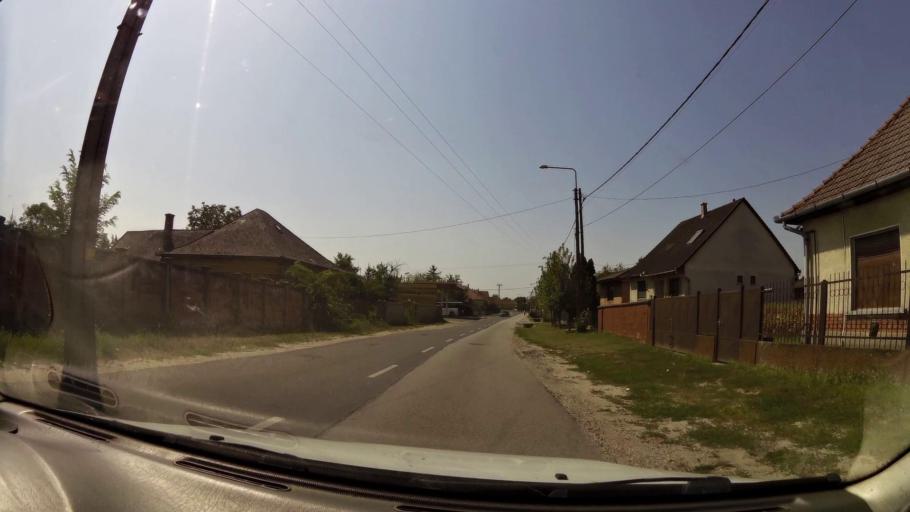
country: HU
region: Pest
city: Tapioszentmarton
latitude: 47.3460
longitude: 19.7477
